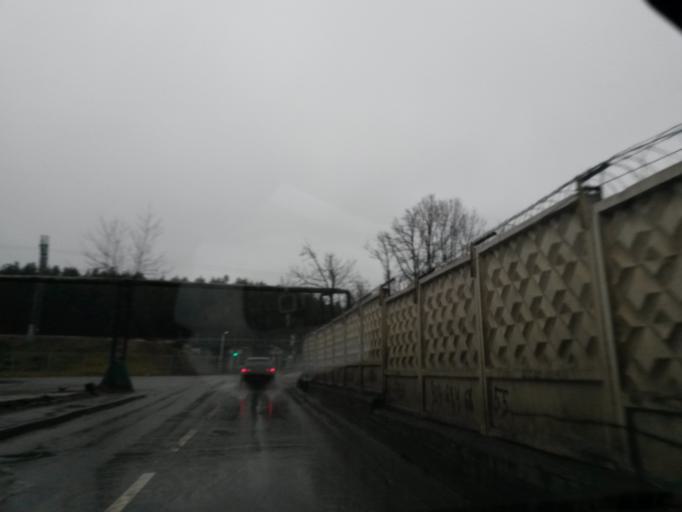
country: RU
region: Moskovskaya
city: Zarech'ye
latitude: 55.6615
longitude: 37.4086
